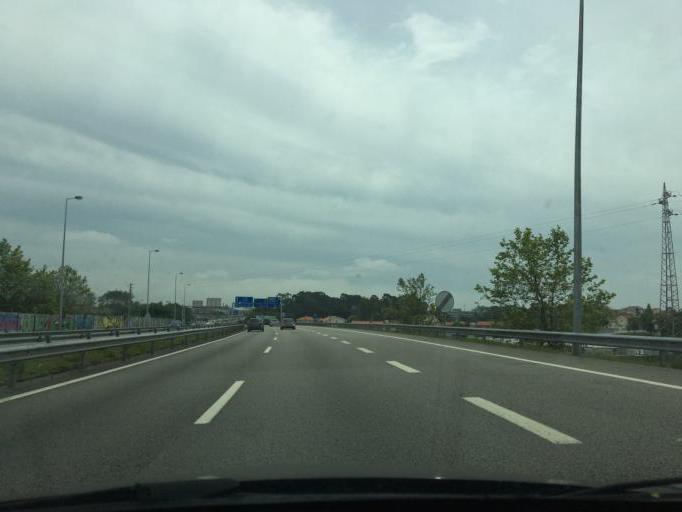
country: PT
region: Porto
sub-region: Matosinhos
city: Santa Cruz do Bispo
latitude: 41.2264
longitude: -8.6947
